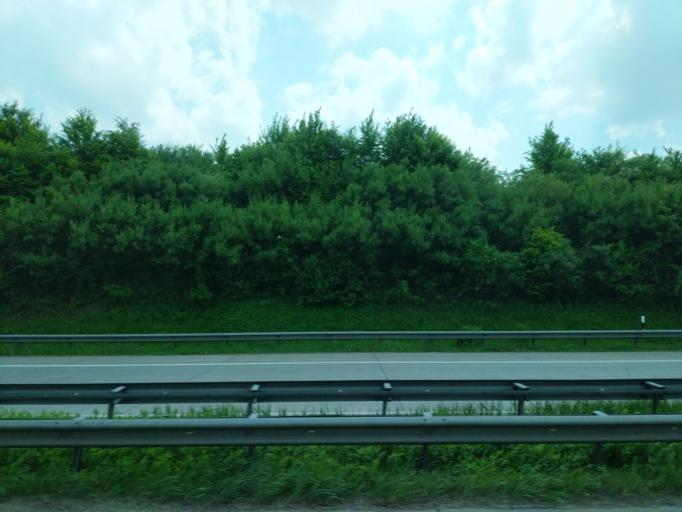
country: DE
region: Schleswig-Holstein
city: Reinbek
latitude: 53.5621
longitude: 10.2473
